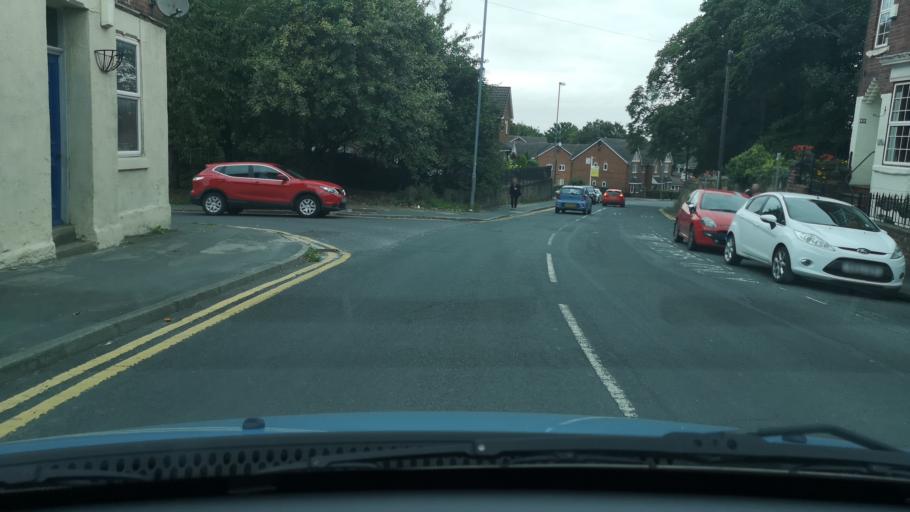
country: GB
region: England
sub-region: City and Borough of Wakefield
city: Pontefract
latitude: 53.6955
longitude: -1.3059
